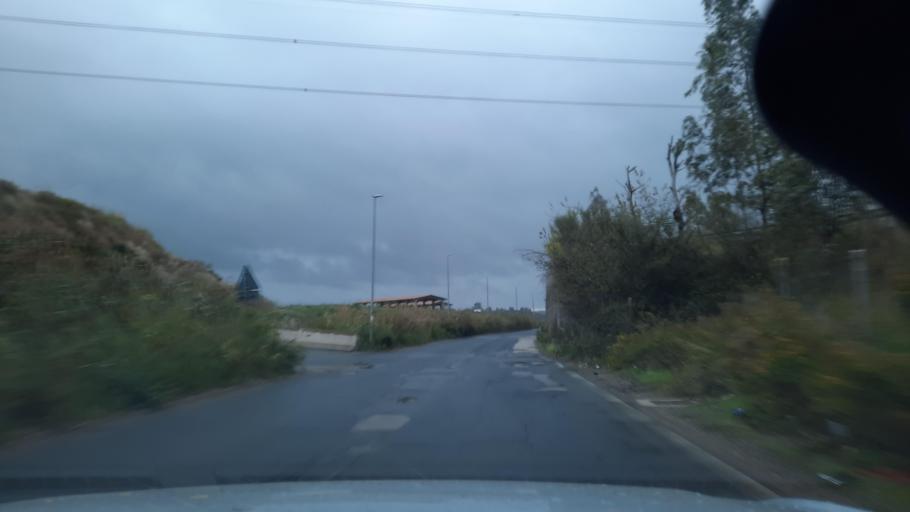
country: IT
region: Latium
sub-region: Citta metropolitana di Roma Capitale
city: Ponte Galeria-La Pisana
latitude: 41.8194
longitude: 12.3658
